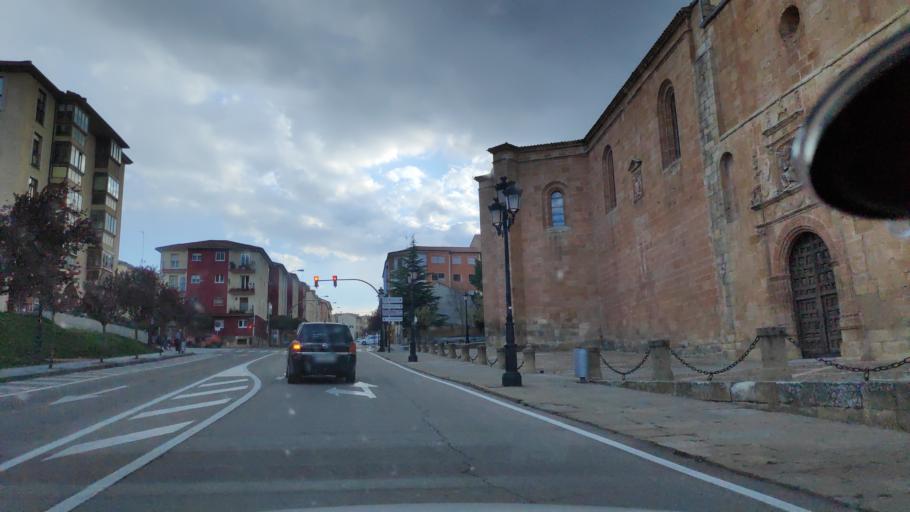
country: ES
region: Castille and Leon
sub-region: Provincia de Soria
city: Soria
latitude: 41.7660
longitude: -2.4585
